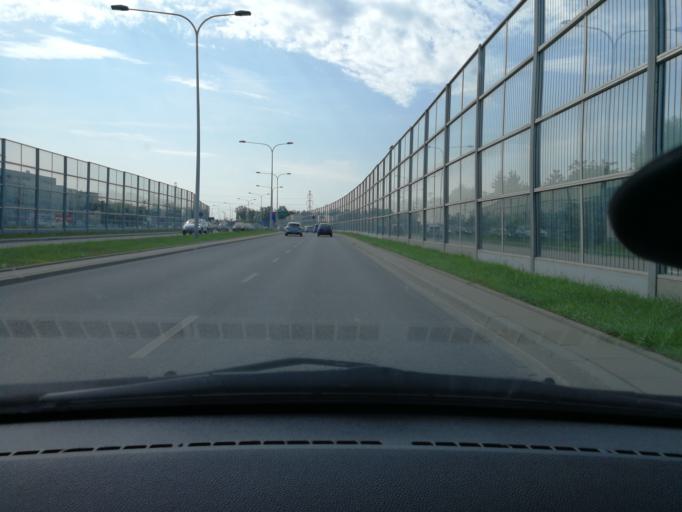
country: PL
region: Masovian Voivodeship
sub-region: Warszawa
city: Ursus
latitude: 52.2197
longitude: 20.8965
